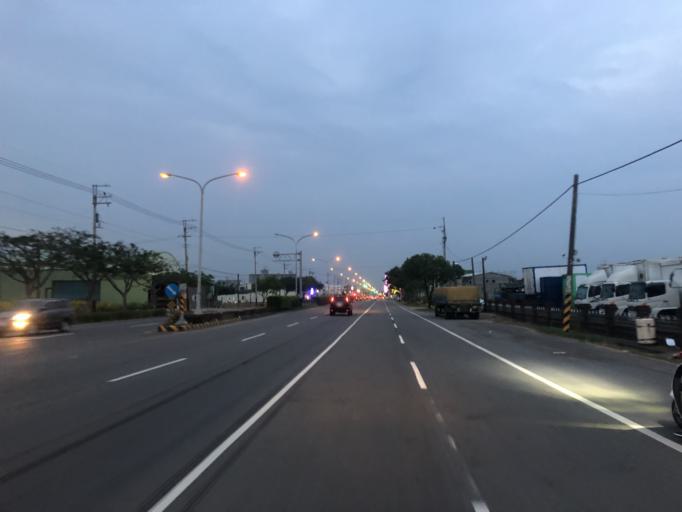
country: TW
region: Taiwan
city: Yujing
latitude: 23.1333
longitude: 120.3212
